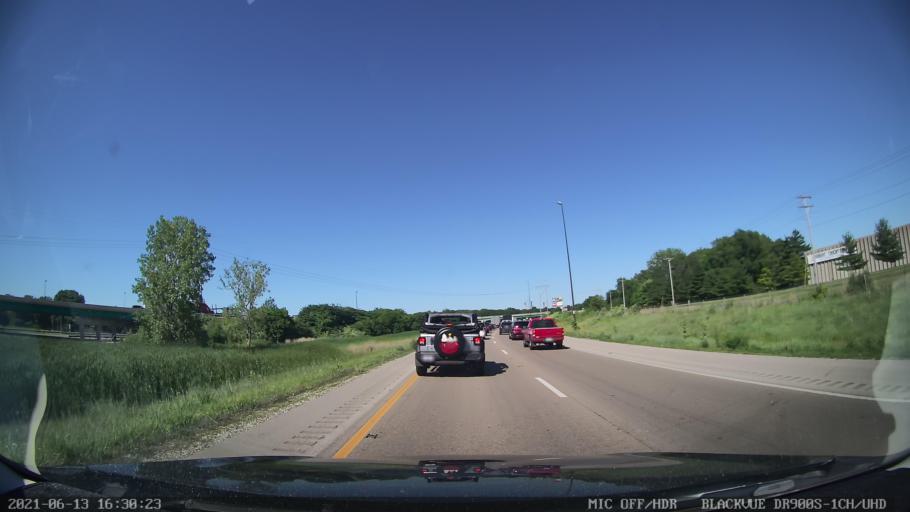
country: US
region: Illinois
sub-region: Sangamon County
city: Southern View
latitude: 39.7408
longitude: -89.6389
